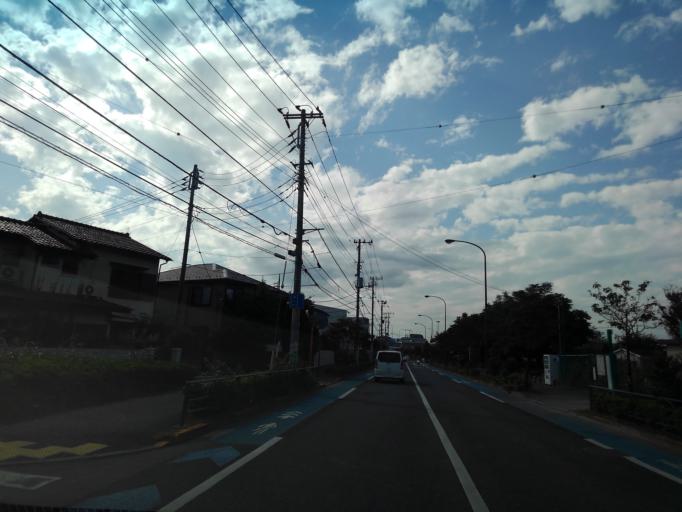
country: JP
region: Tokyo
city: Chofugaoka
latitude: 35.6628
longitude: 139.5328
